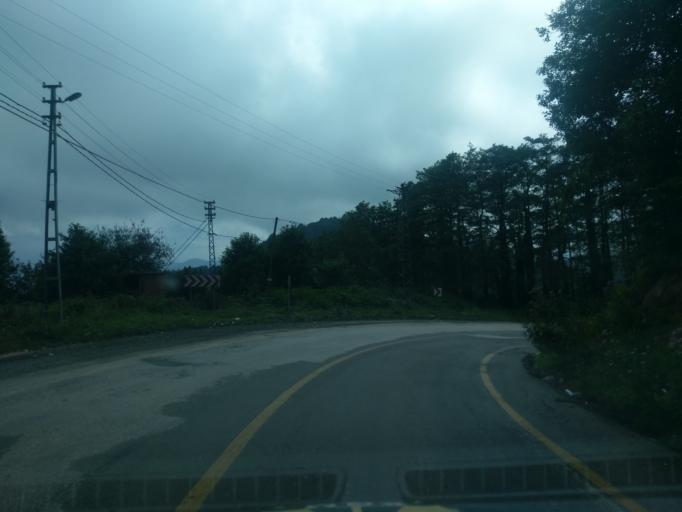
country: TR
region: Ordu
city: Gurgentepe
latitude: 40.8484
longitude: 37.6551
